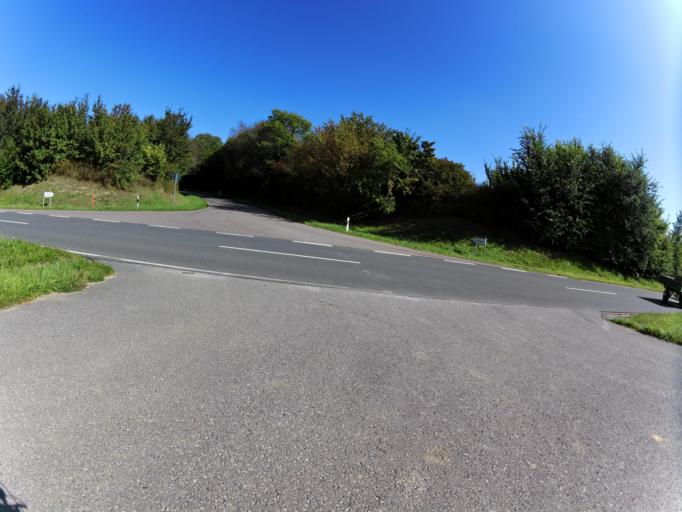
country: DE
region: Bavaria
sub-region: Regierungsbezirk Unterfranken
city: Kleinrinderfeld
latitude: 49.6951
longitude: 9.7883
